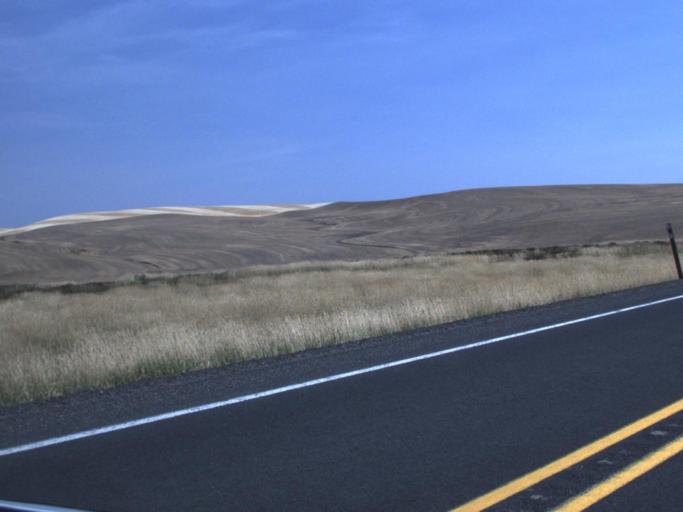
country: US
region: Washington
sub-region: Whitman County
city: Colfax
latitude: 47.1783
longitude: -117.1943
